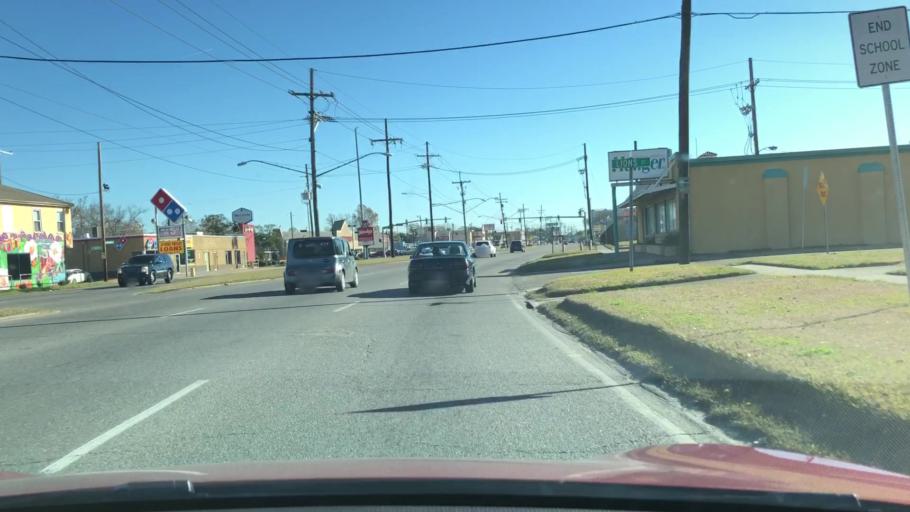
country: US
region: Louisiana
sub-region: Jefferson Parish
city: Jefferson
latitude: 29.9631
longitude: -90.1653
